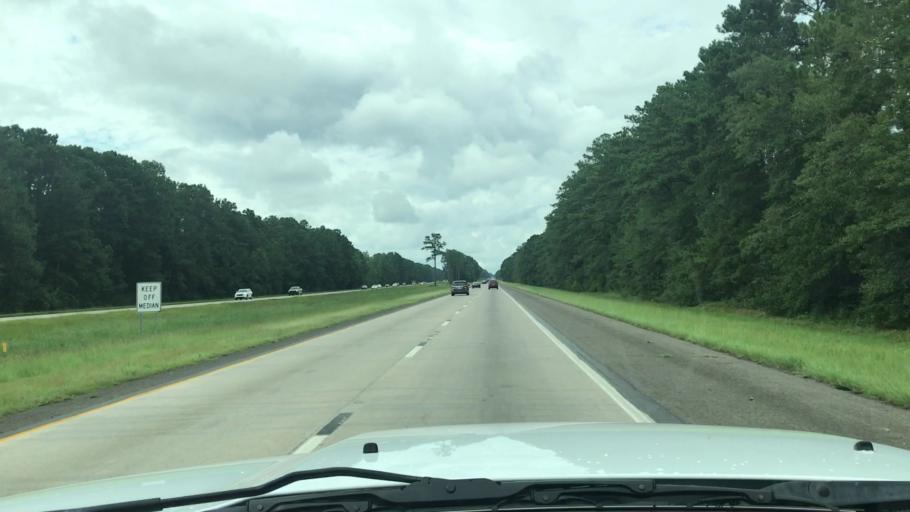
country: US
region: South Carolina
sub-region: Colleton County
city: Walterboro
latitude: 32.8428
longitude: -80.7383
